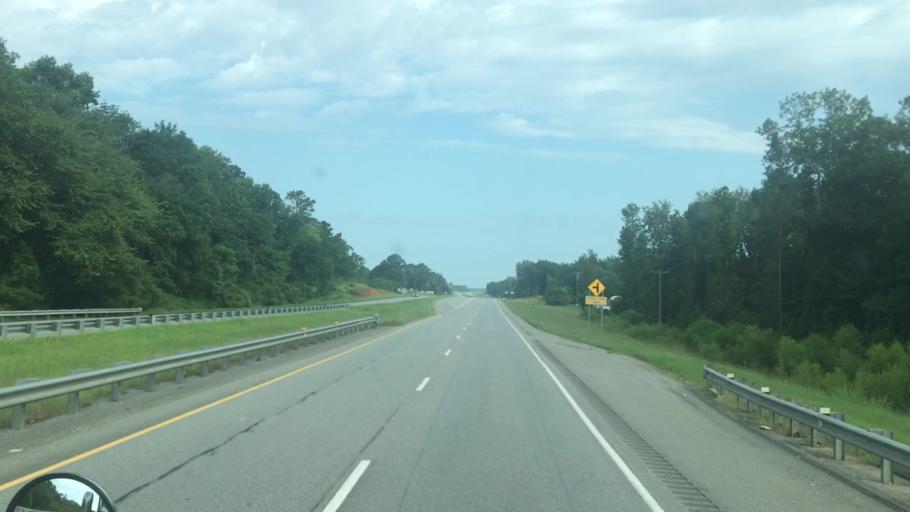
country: US
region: Georgia
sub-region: Early County
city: Blakely
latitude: 31.3334
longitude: -84.8967
